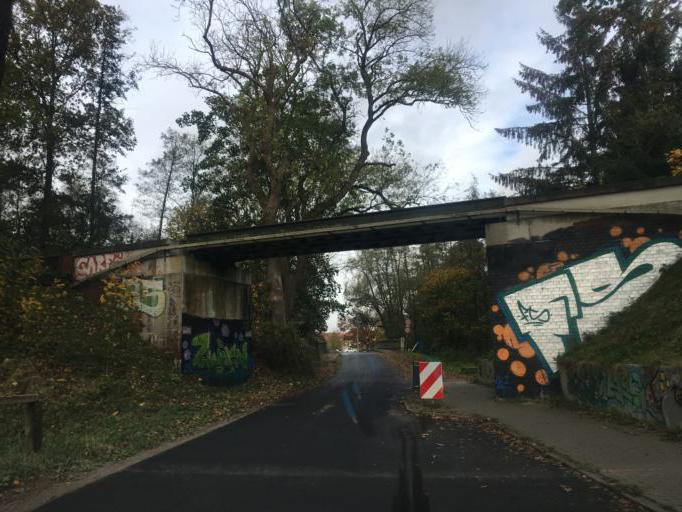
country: DE
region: Lower Saxony
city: Lueneburg
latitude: 53.2332
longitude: 10.4122
